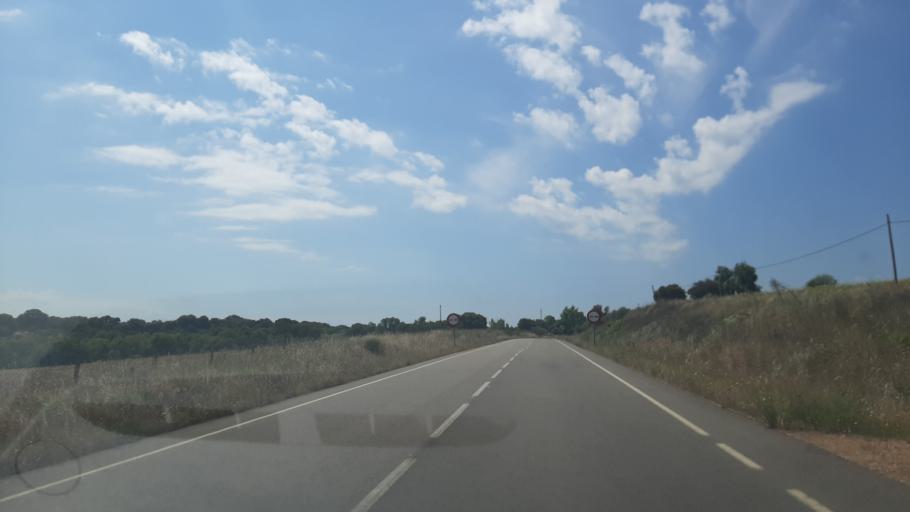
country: ES
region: Castille and Leon
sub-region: Provincia de Salamanca
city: Gallegos de Arganan
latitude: 40.6009
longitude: -6.7044
